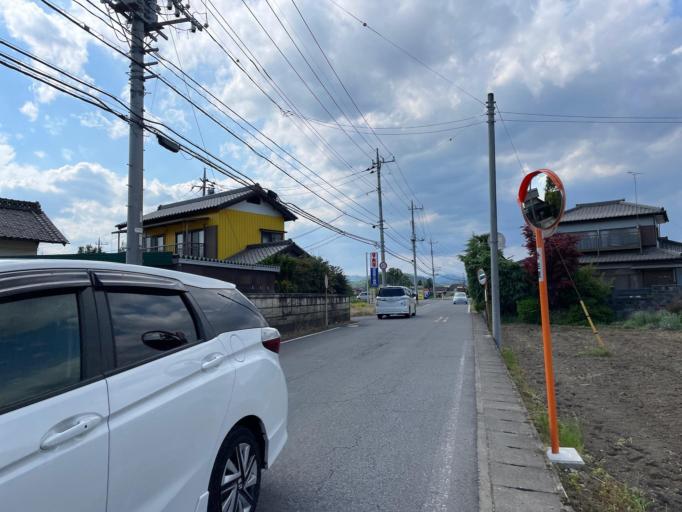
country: JP
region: Tochigi
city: Tochigi
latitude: 36.4114
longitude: 139.7343
